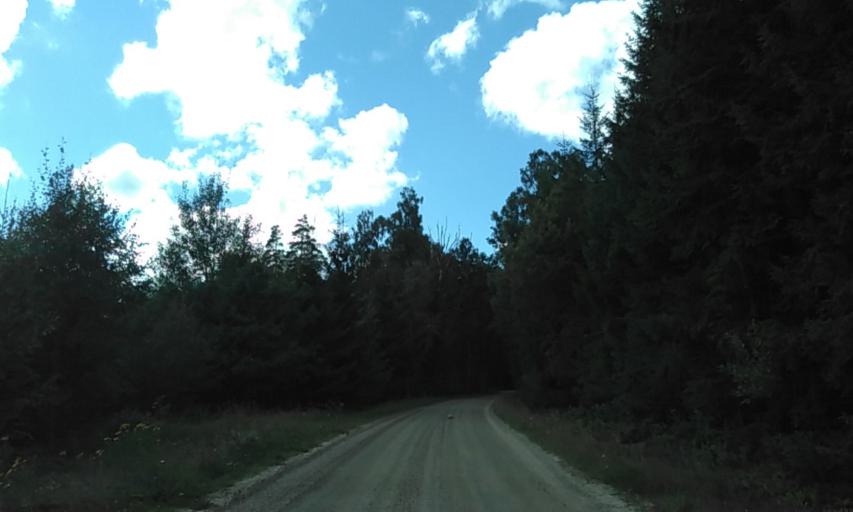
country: SE
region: Vaestra Goetaland
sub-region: Vargarda Kommun
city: Vargarda
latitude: 58.0028
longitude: 12.8970
